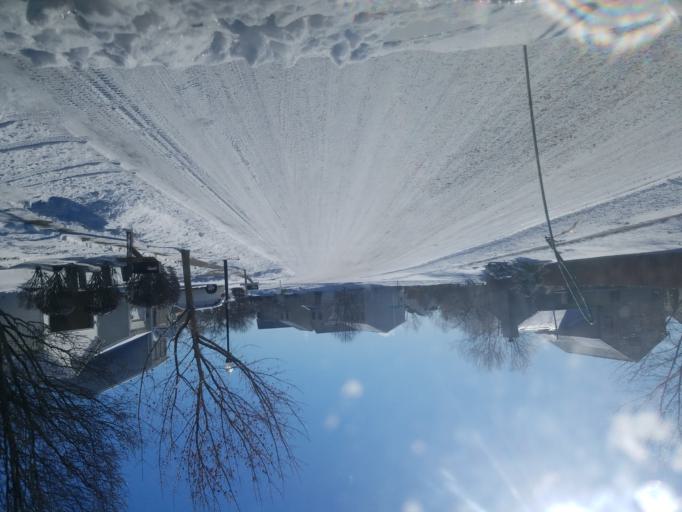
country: US
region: Ohio
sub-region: Franklin County
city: Worthington
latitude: 40.1422
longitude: -83.0099
